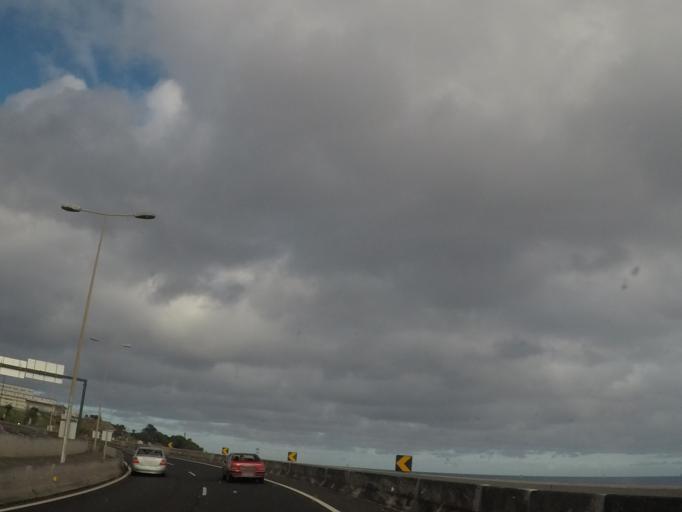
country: PT
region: Madeira
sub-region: Santa Cruz
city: Santa Cruz
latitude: 32.6880
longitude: -16.7845
